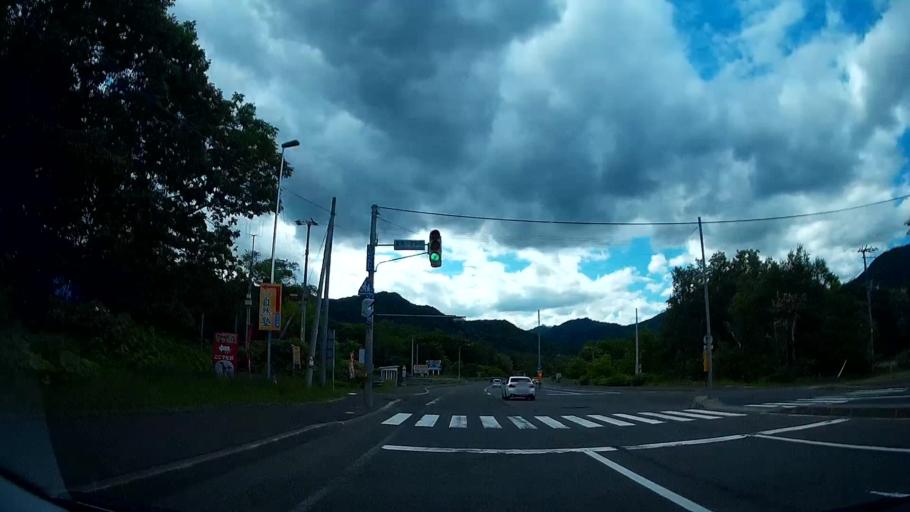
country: JP
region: Hokkaido
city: Sapporo
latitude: 42.9576
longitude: 141.2307
